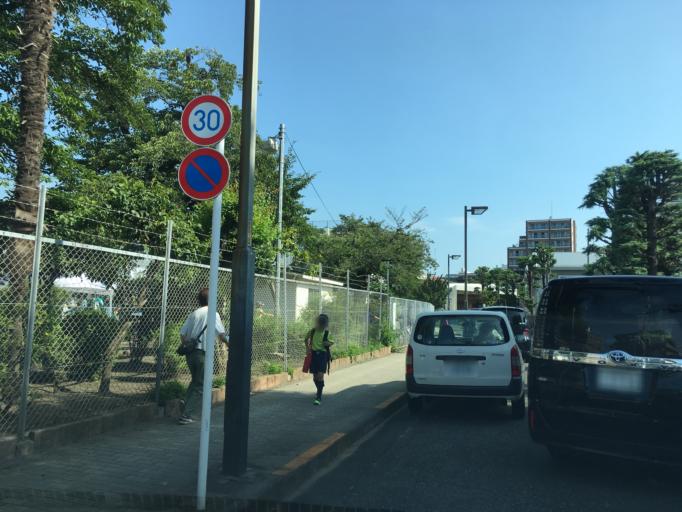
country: JP
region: Tokyo
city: Fussa
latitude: 35.7159
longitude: 139.3445
